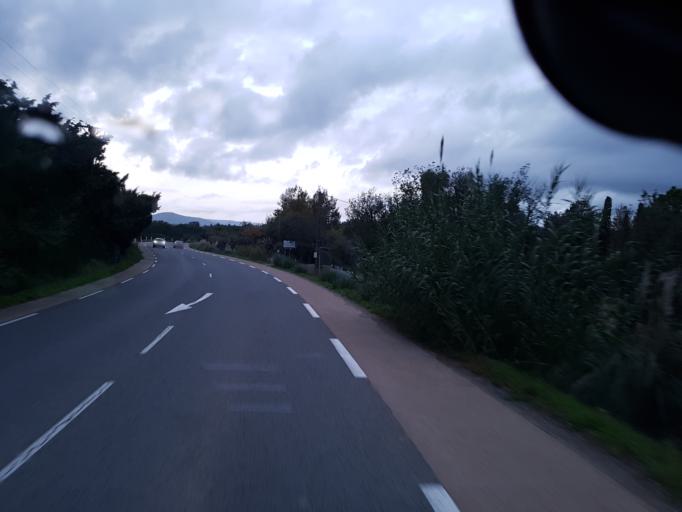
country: FR
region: Provence-Alpes-Cote d'Azur
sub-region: Departement du Var
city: Grimaud
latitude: 43.2698
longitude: 6.5452
